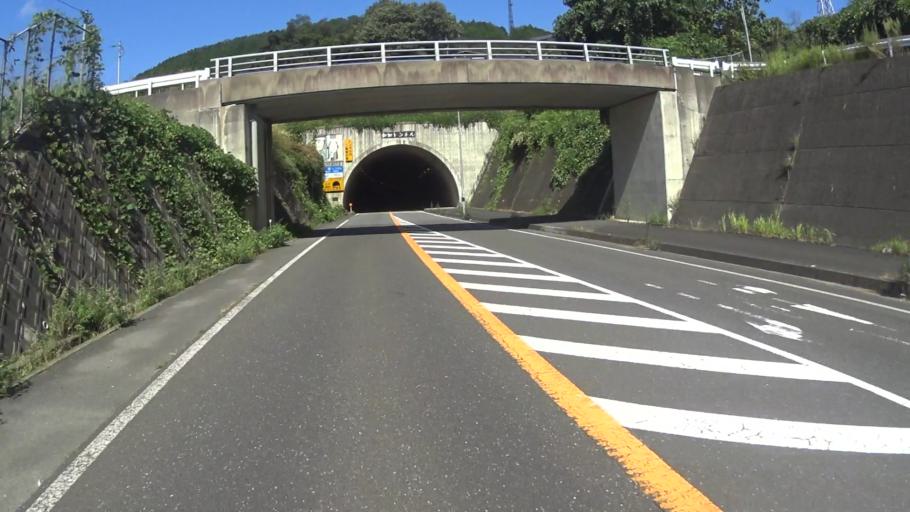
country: JP
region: Kyoto
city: Ayabe
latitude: 35.2614
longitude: 135.4068
